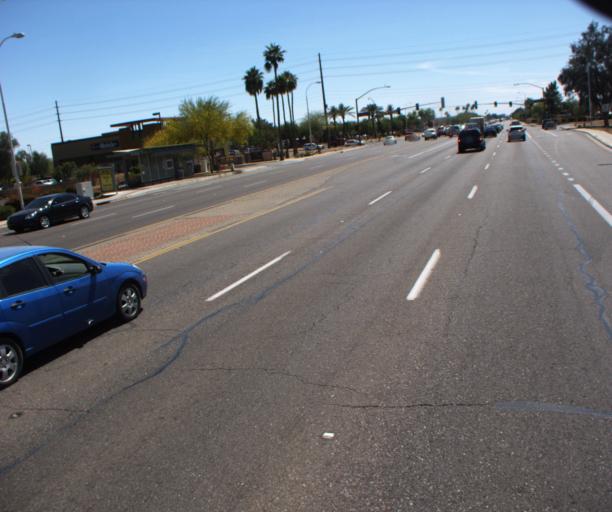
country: US
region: Arizona
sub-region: Maricopa County
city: San Carlos
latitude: 33.3364
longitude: -111.8419
